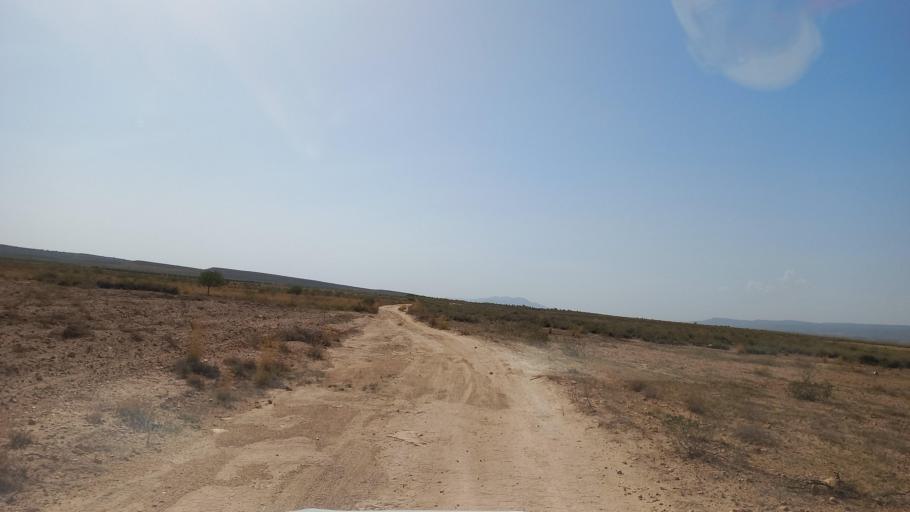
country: TN
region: Al Qasrayn
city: Kasserine
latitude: 35.2167
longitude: 9.0271
